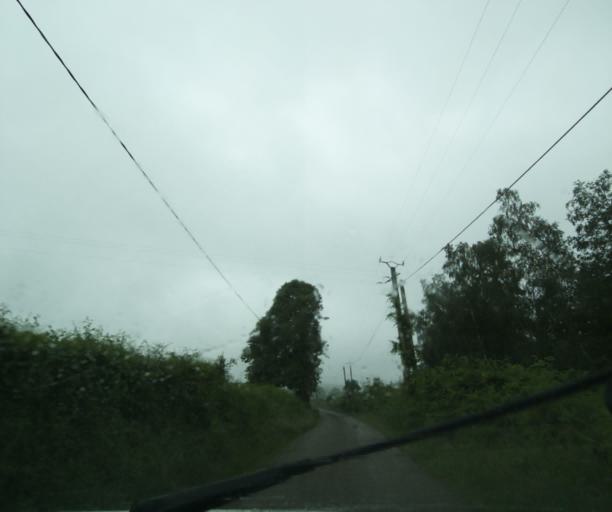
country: FR
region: Bourgogne
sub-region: Departement de Saone-et-Loire
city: Charolles
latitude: 46.3750
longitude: 4.3464
